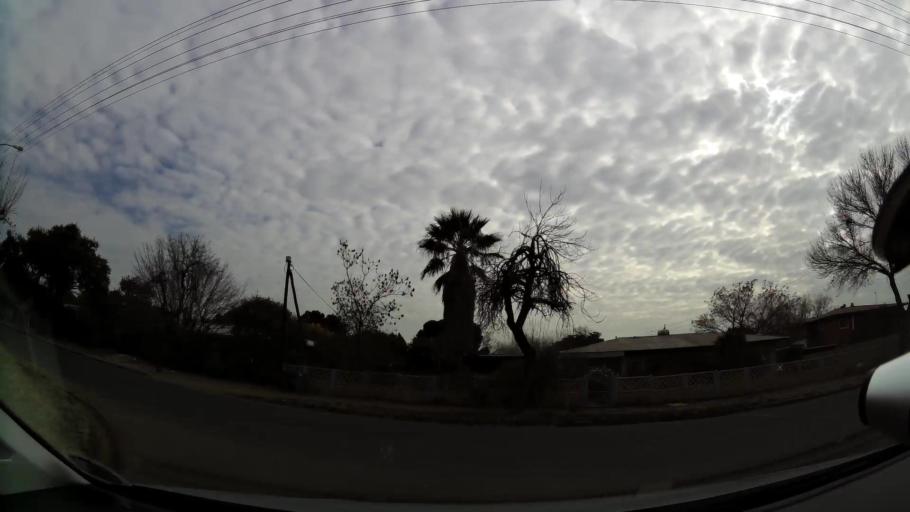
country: ZA
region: Orange Free State
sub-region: Mangaung Metropolitan Municipality
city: Bloemfontein
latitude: -29.1274
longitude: 26.1895
